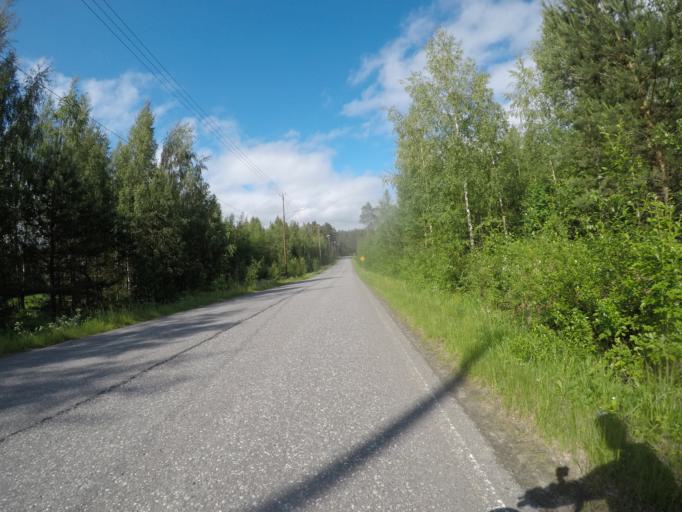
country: FI
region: Haeme
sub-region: Haemeenlinna
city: Haemeenlinna
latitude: 60.9690
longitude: 24.4247
